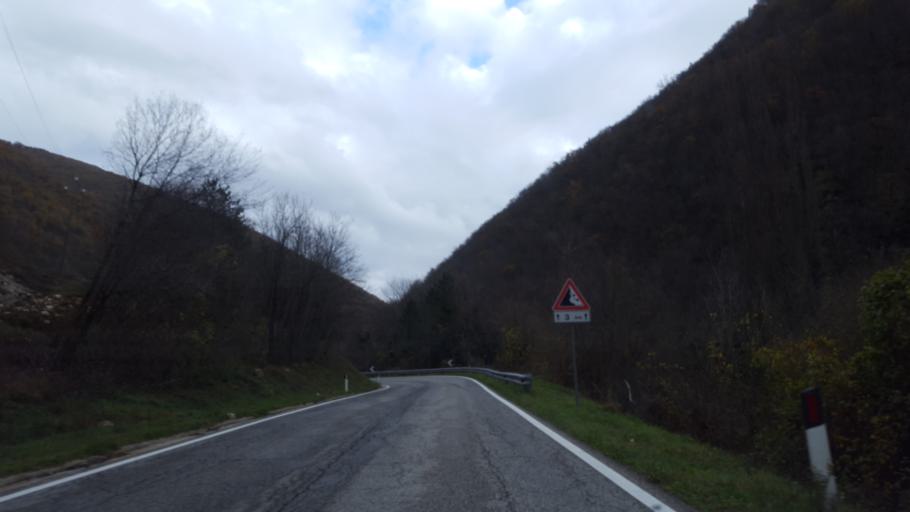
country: IT
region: The Marches
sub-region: Provincia di Macerata
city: Fluminata
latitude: 42.9149
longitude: 13.1242
